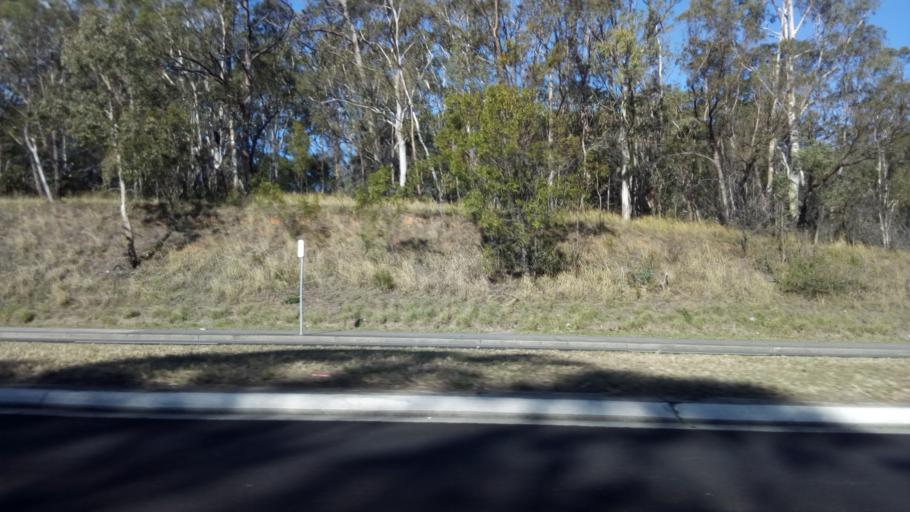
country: AU
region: New South Wales
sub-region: Shellharbour
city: Barrack Heights
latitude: -34.5654
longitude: 150.8269
